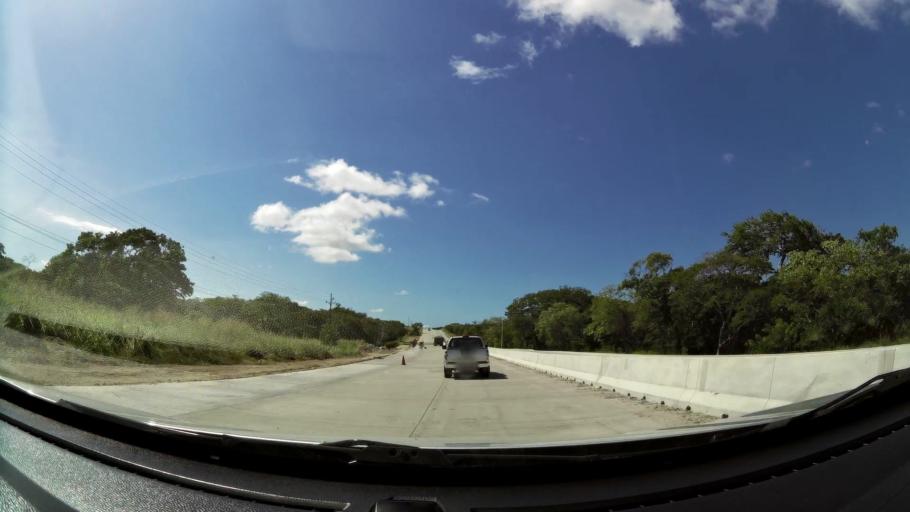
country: CR
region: Guanacaste
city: Bagaces
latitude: 10.5398
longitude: -85.3054
